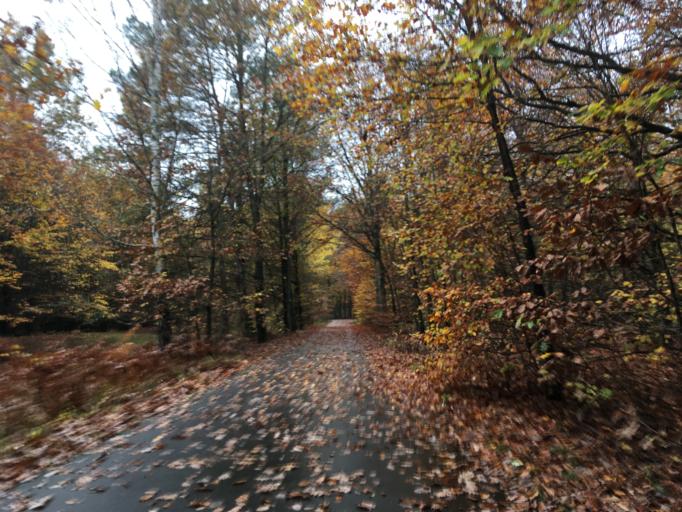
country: DE
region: Brandenburg
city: Briesen
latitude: 52.3062
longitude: 14.2205
